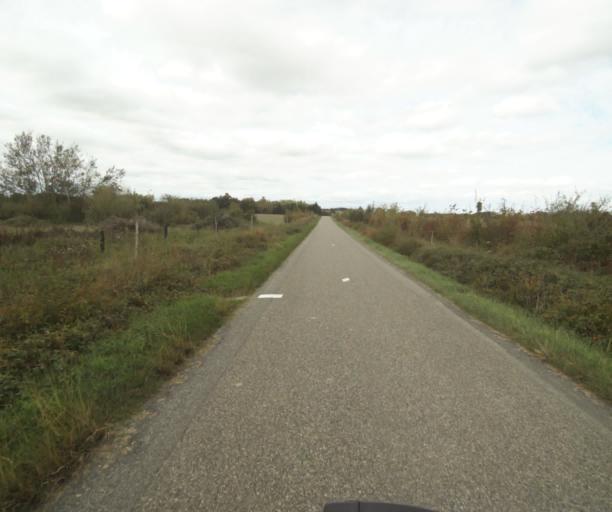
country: FR
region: Midi-Pyrenees
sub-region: Departement du Tarn-et-Garonne
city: Finhan
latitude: 43.8723
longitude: 1.1493
